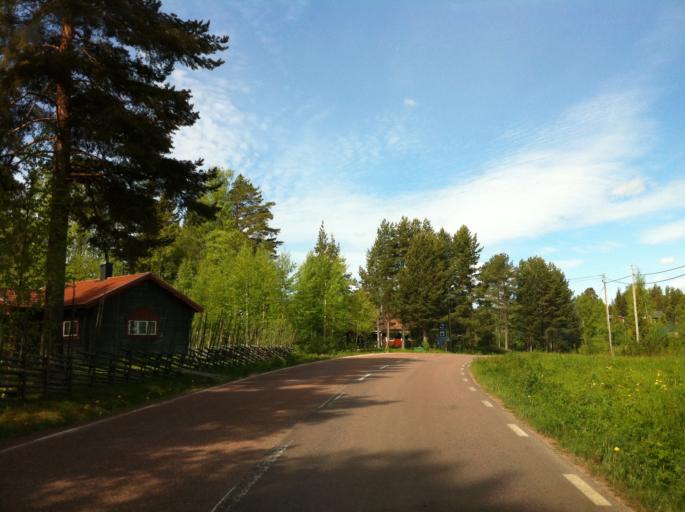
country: SE
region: Dalarna
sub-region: Mora Kommun
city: Mora
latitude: 60.8833
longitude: 14.5661
